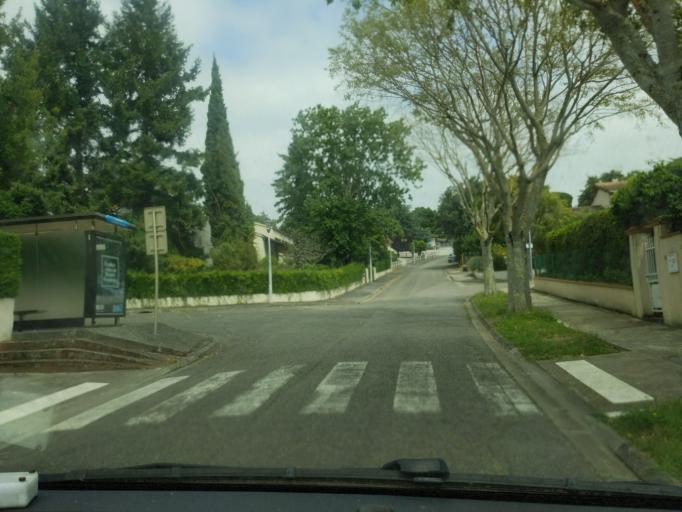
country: FR
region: Midi-Pyrenees
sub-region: Departement de la Haute-Garonne
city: Labege
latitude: 43.5290
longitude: 1.5401
